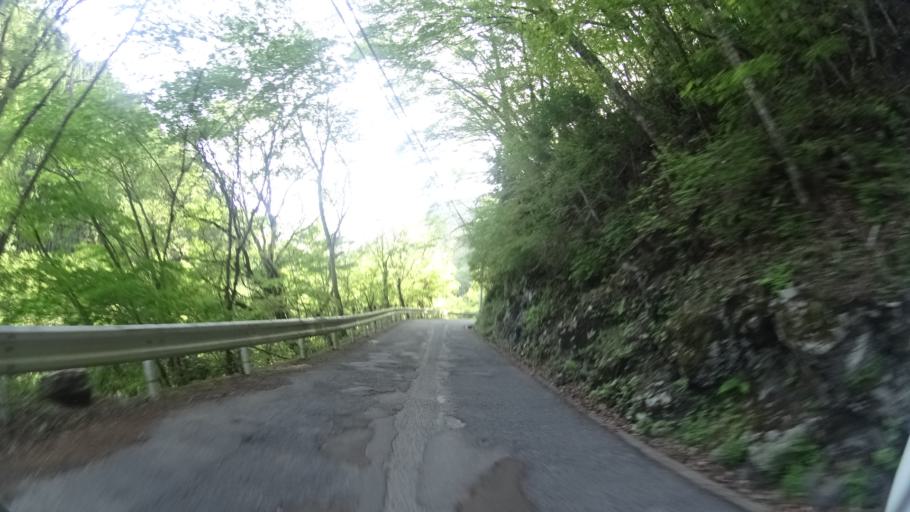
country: JP
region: Tokushima
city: Ikedacho
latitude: 33.8729
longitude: 133.9791
